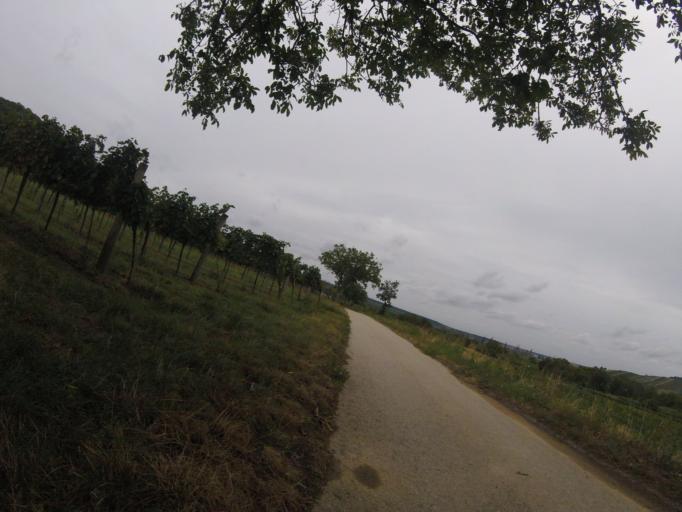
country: AT
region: Burgenland
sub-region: Politischer Bezirk Neusiedl am See
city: Winden am See
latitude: 47.9691
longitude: 16.7656
